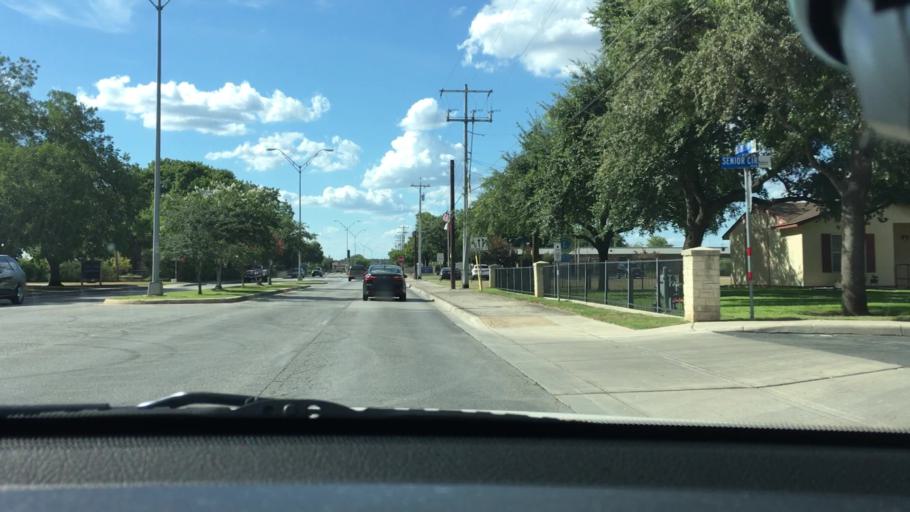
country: US
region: Texas
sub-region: Guadalupe County
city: Schertz
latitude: 29.5566
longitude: -98.2645
